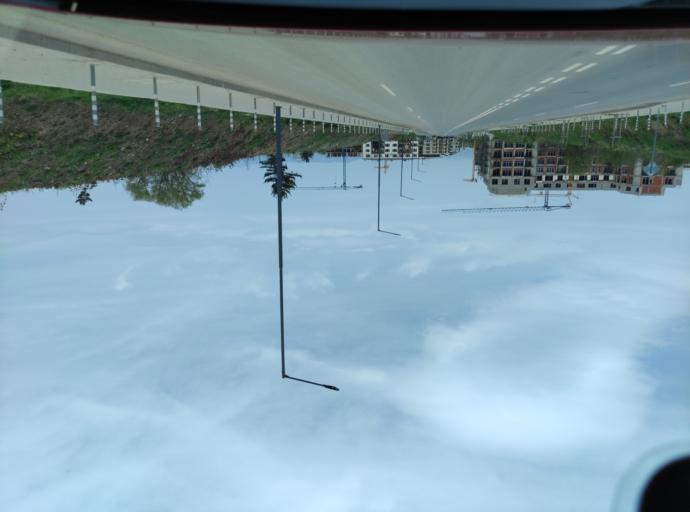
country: BG
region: Sofia-Capital
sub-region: Stolichna Obshtina
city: Sofia
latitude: 42.6386
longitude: 23.3423
